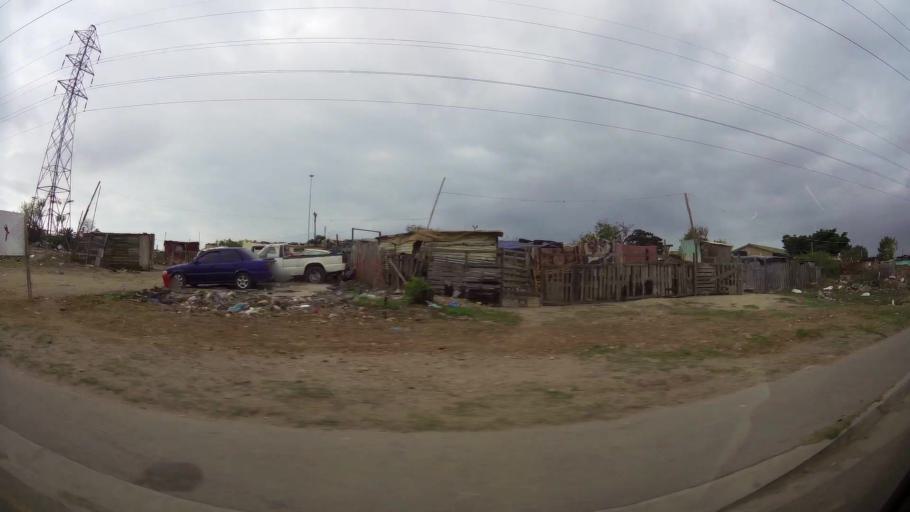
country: ZA
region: Eastern Cape
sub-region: Nelson Mandela Bay Metropolitan Municipality
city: Port Elizabeth
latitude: -33.8812
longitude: 25.5843
